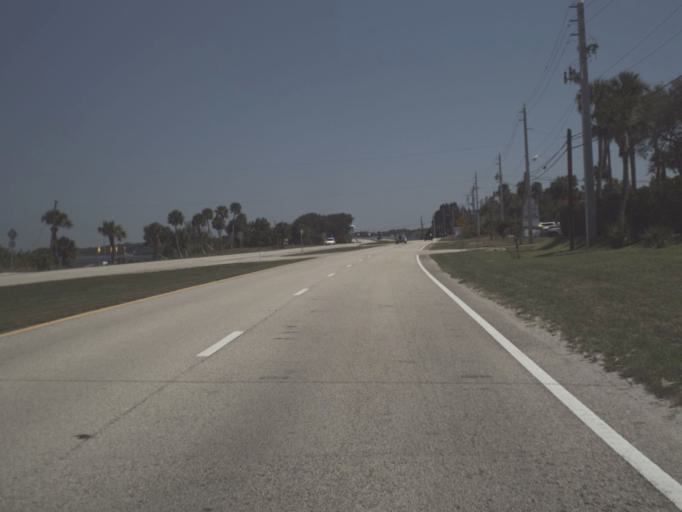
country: US
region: Florida
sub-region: Brevard County
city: Micco
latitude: 27.8609
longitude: -80.4925
